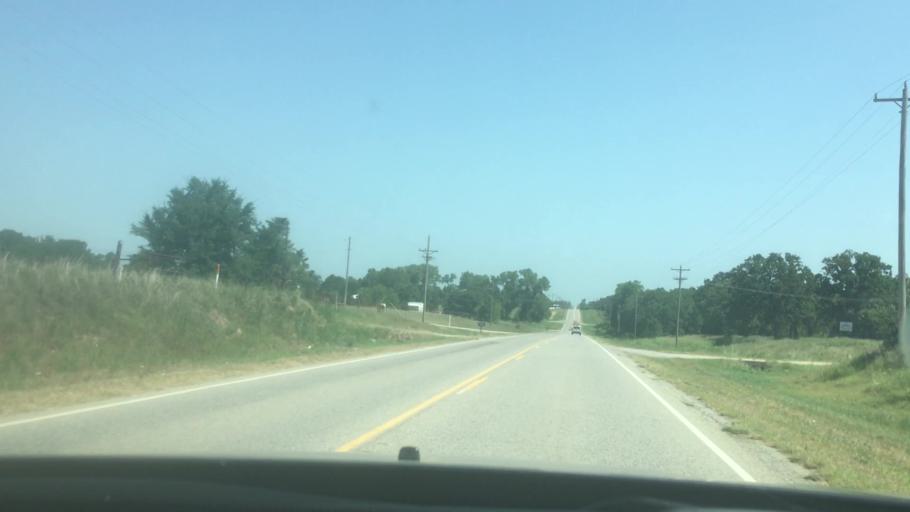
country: US
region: Oklahoma
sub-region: Bryan County
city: Durant
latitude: 34.2400
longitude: -96.4248
